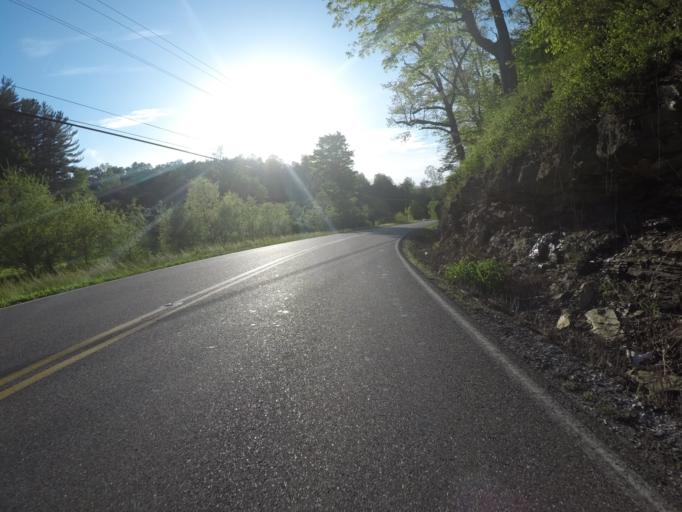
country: US
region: West Virginia
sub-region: Cabell County
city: Huntington
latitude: 38.5514
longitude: -82.4409
